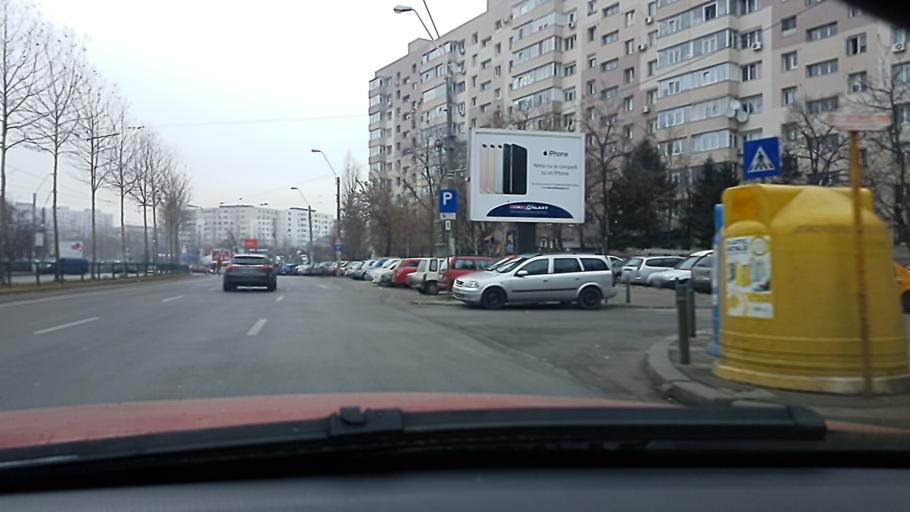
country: RO
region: Ilfov
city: Dobroesti
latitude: 44.4180
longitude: 26.1763
